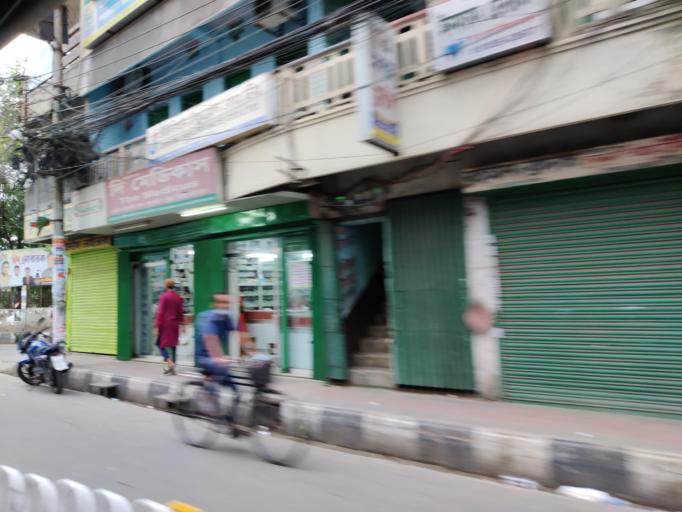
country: BD
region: Barisal
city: Barisal
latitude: 22.7065
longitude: 90.3709
